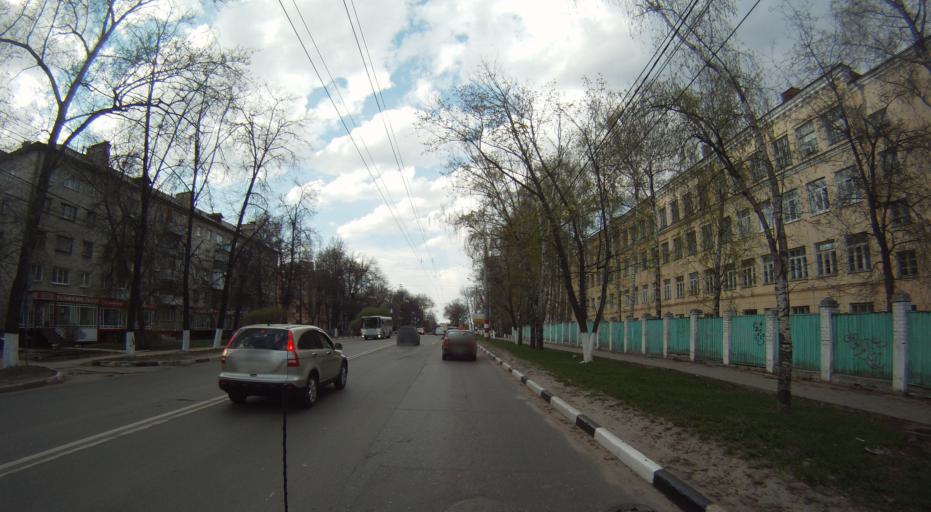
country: RU
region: Nizjnij Novgorod
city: Nizhniy Novgorod
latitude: 56.3121
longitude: 44.0199
